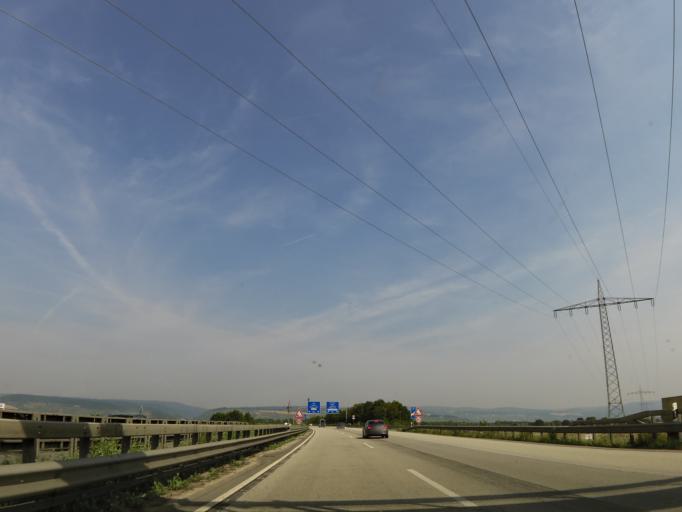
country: DE
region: Rheinland-Pfalz
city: Gensingen
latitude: 49.9225
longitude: 7.9458
